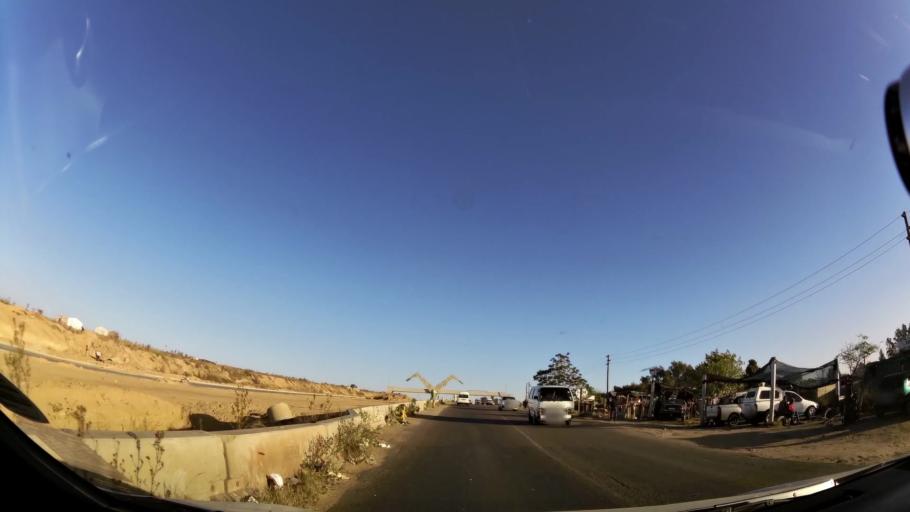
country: ZA
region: Gauteng
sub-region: City of Johannesburg Metropolitan Municipality
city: Diepsloot
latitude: -25.9274
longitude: 28.0222
